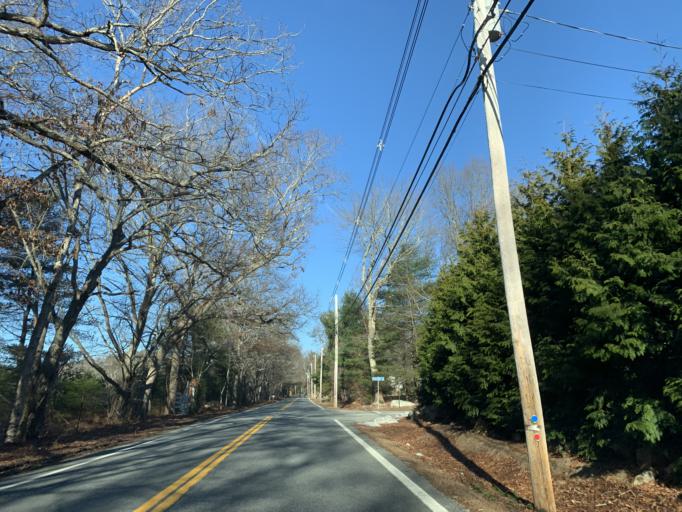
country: US
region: Rhode Island
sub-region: Washington County
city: Exeter
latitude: 41.5714
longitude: -71.5356
